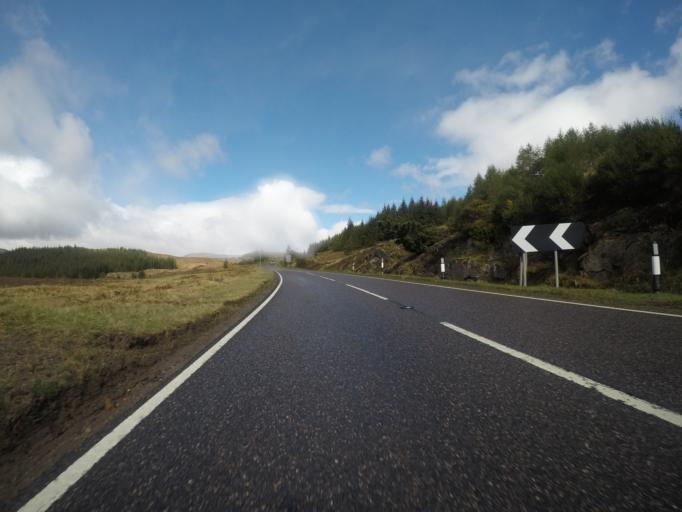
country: GB
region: Scotland
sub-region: Highland
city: Spean Bridge
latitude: 57.0900
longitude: -4.9819
